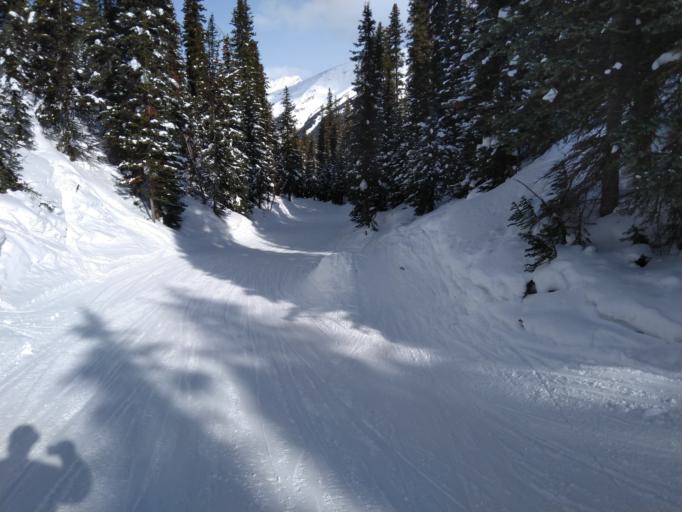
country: CA
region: Alberta
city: Banff
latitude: 51.0920
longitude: -115.7700
